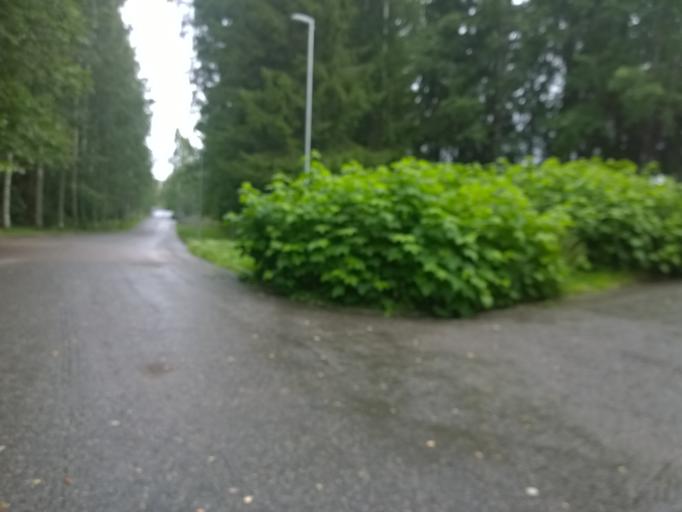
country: FI
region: Pirkanmaa
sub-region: Tampere
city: Tampere
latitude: 61.4492
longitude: 23.8367
